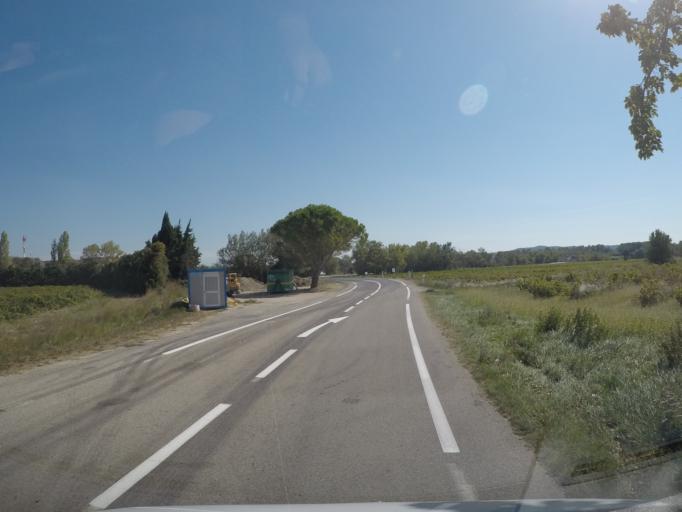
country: FR
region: Languedoc-Roussillon
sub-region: Departement du Gard
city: Tavel
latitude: 44.0078
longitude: 4.7332
